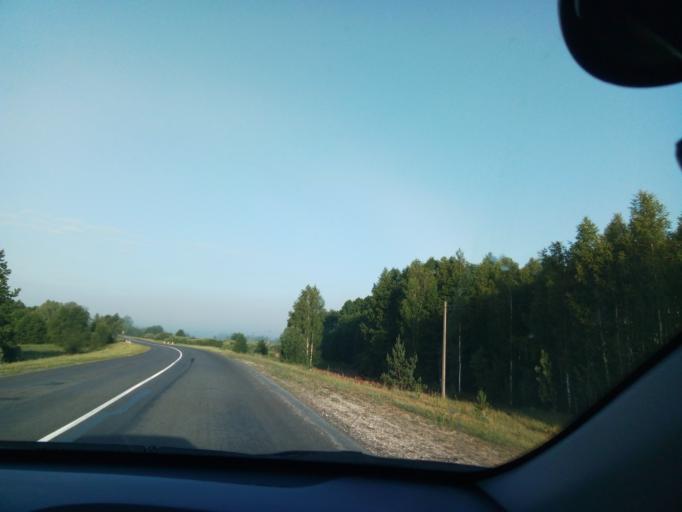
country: RU
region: Nizjnij Novgorod
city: Voznesenskoye
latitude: 54.8673
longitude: 42.9542
